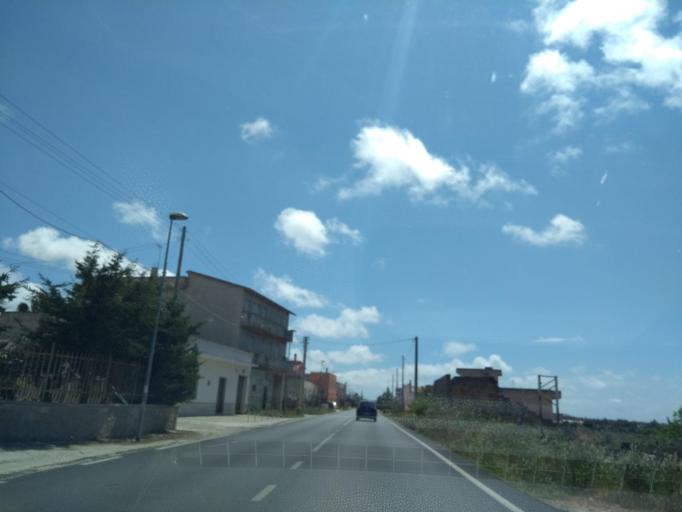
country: IT
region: Sicily
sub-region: Trapani
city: Marsala
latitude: 37.8591
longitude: 12.5153
